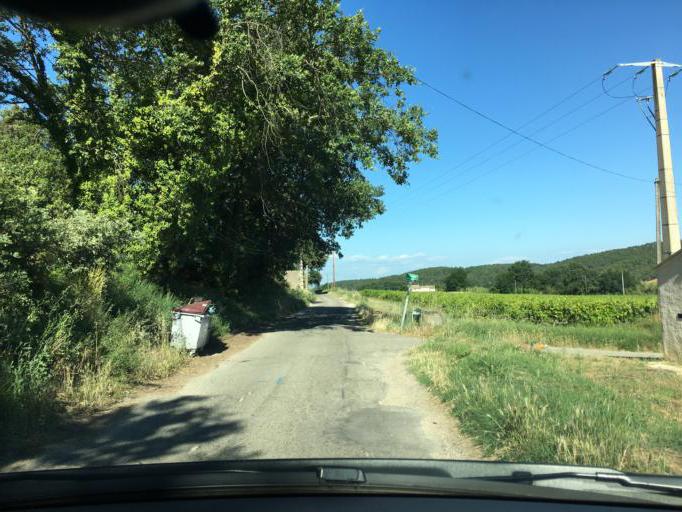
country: FR
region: Provence-Alpes-Cote d'Azur
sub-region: Departement du Vaucluse
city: Bollene
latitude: 44.3040
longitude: 4.7598
